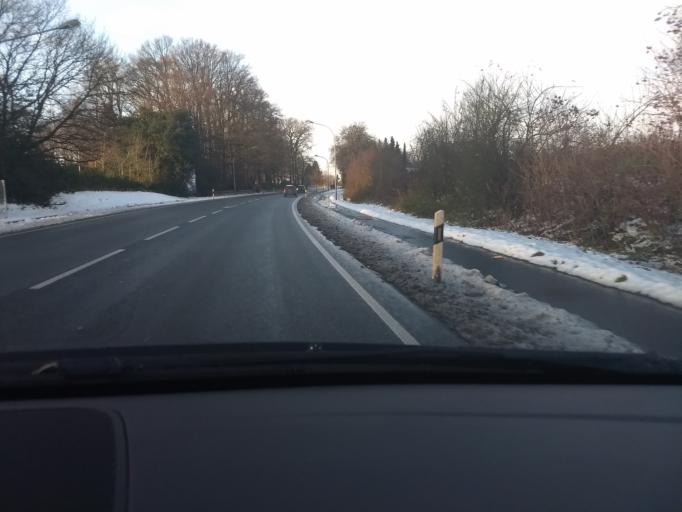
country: DE
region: Lower Saxony
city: Nordhorn
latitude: 52.4509
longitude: 7.0494
